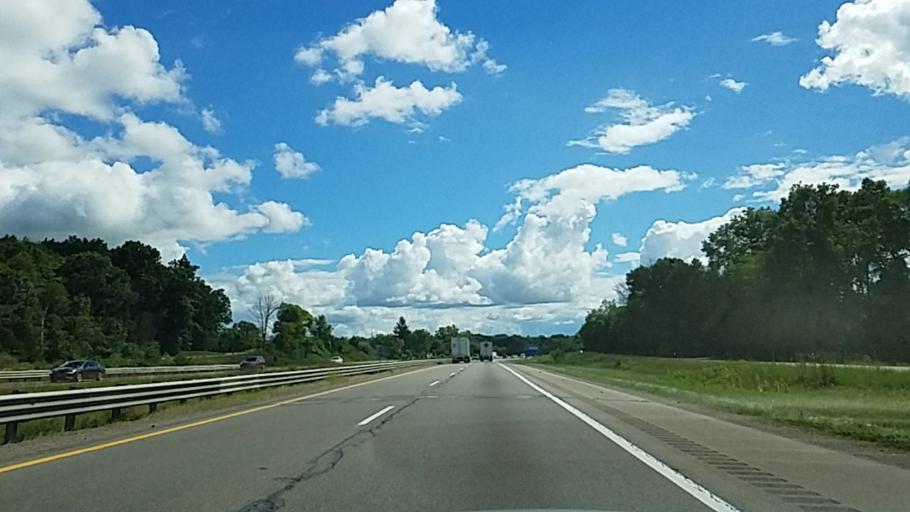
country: US
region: Michigan
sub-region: Livingston County
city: Whitmore Lake
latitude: 42.4584
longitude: -83.7540
